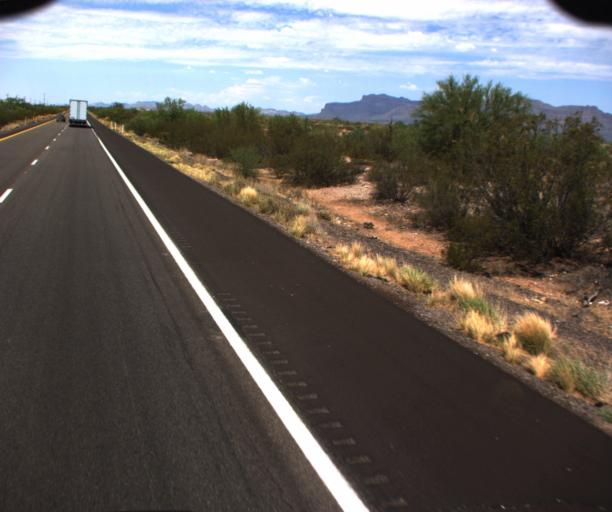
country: US
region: Arizona
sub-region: Pinal County
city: Gold Camp
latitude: 33.2835
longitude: -111.3732
